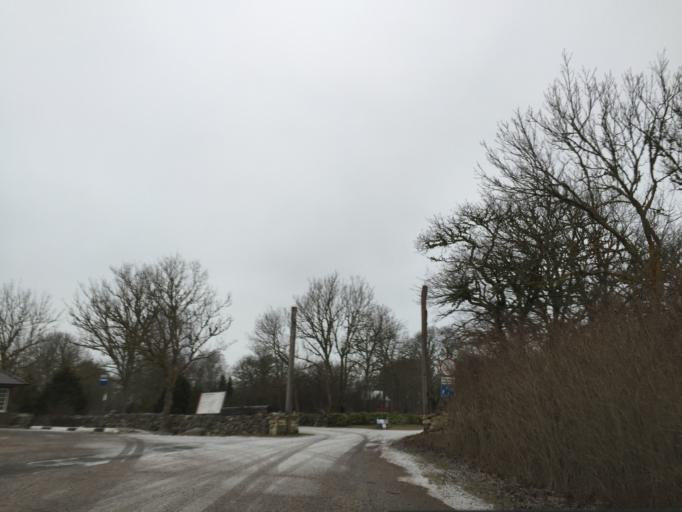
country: EE
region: Saare
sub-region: Orissaare vald
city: Orissaare
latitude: 58.5954
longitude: 23.0836
